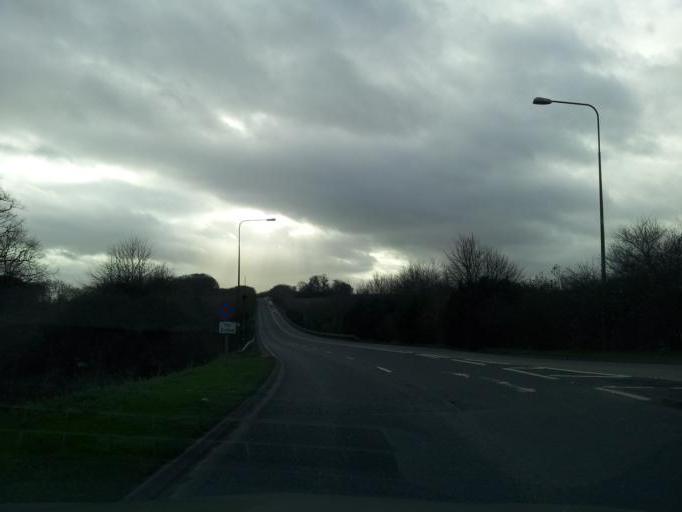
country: GB
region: England
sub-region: Lincolnshire
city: Louth
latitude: 53.3646
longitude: -0.0263
